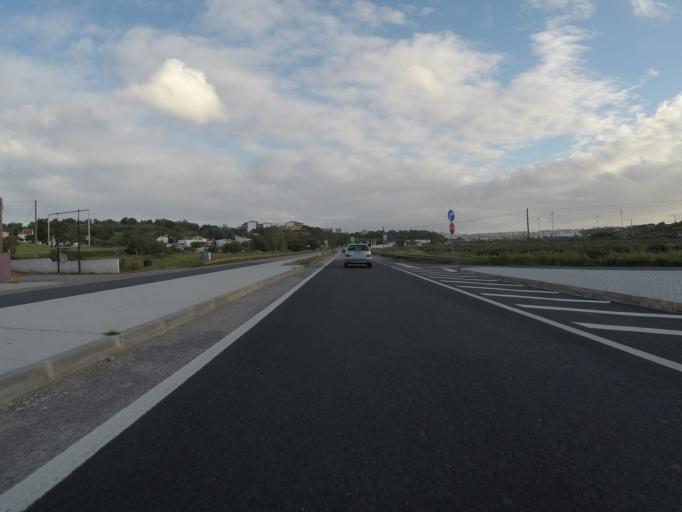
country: PT
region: Faro
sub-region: Lagos
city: Lagos
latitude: 37.1222
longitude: -8.6732
